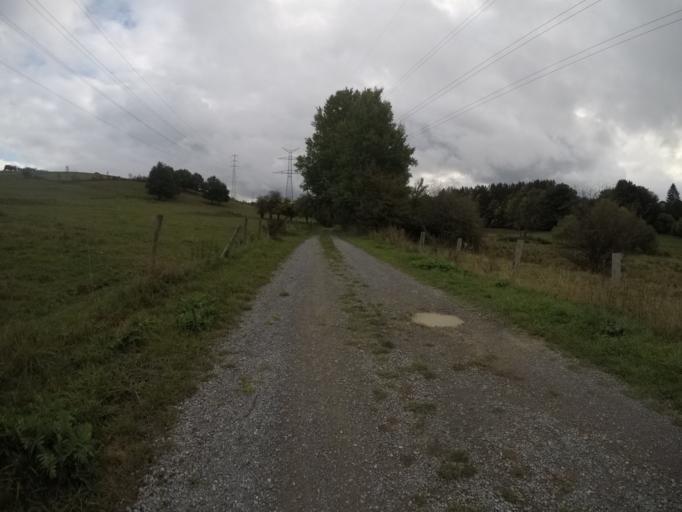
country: BE
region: Wallonia
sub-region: Province du Luxembourg
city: Fauvillers
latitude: 49.9004
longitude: 5.6874
